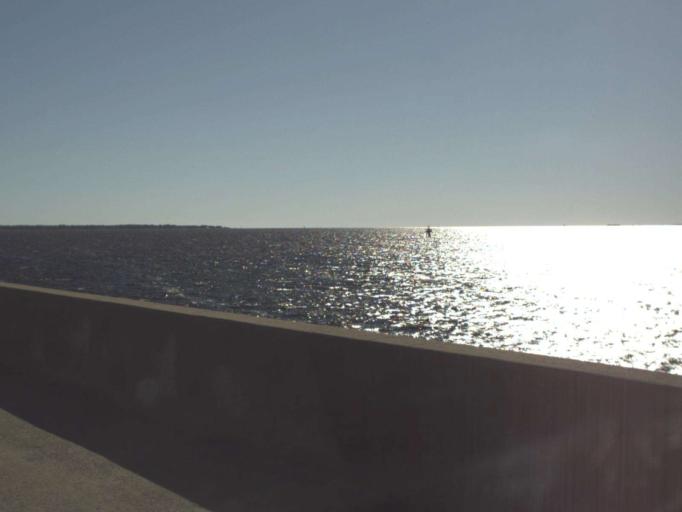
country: US
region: Florida
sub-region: Escambia County
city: East Pensacola Heights
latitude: 30.4111
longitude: -87.1912
